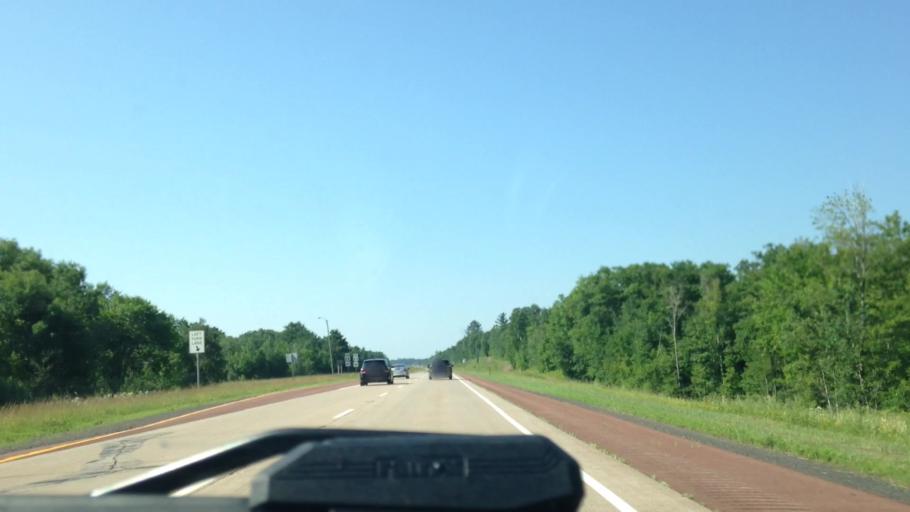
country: US
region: Wisconsin
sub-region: Douglas County
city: Lake Nebagamon
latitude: 46.3831
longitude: -91.8224
